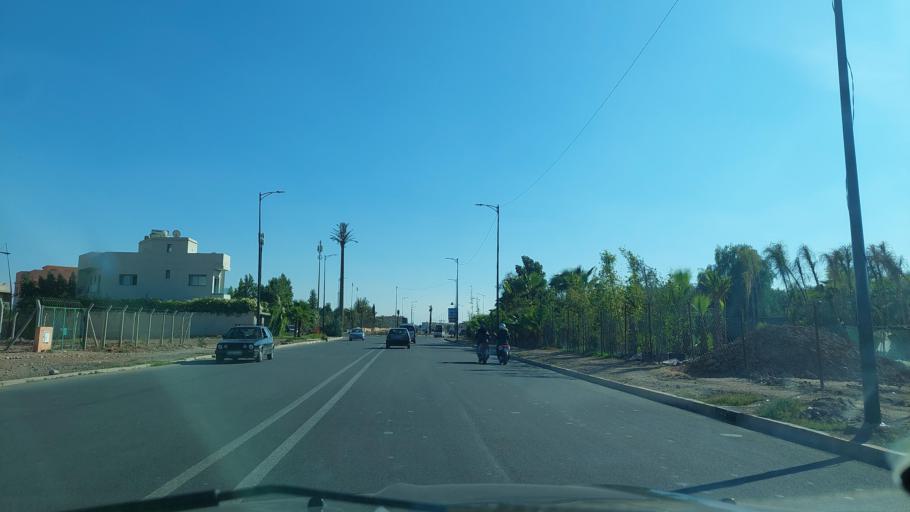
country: MA
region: Marrakech-Tensift-Al Haouz
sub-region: Marrakech
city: Marrakesh
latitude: 31.6549
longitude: -8.0665
